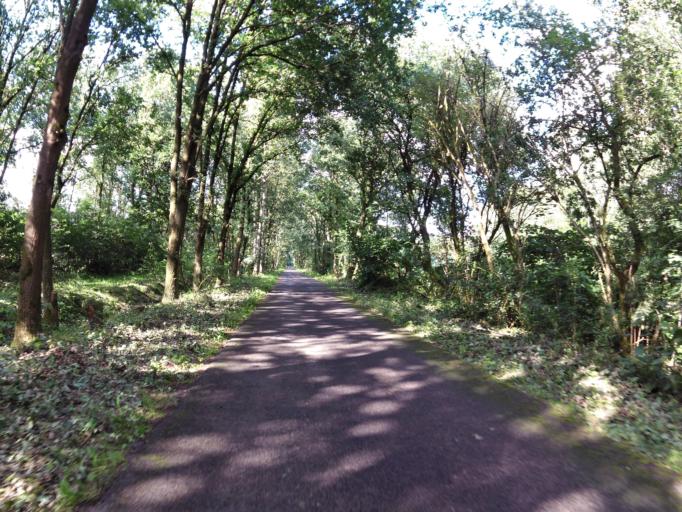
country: NL
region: North Brabant
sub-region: Gemeente Heeze-Leende
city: Heeze
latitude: 51.3795
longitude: 5.5471
